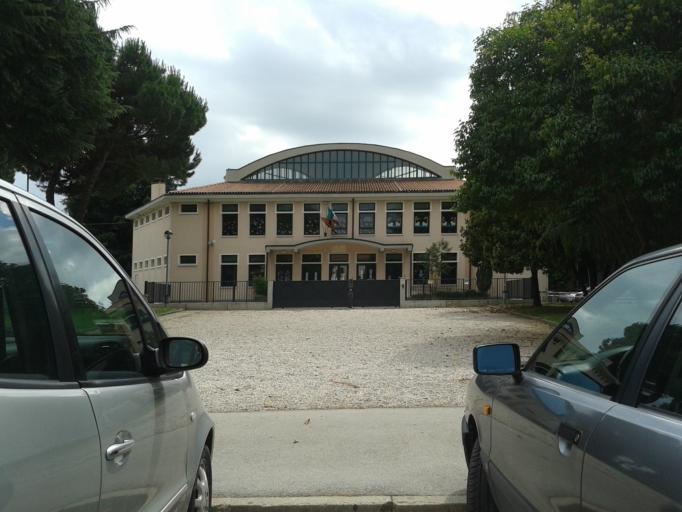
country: IT
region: Veneto
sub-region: Provincia di Padova
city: Villa del Conte
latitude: 45.5834
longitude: 11.8600
